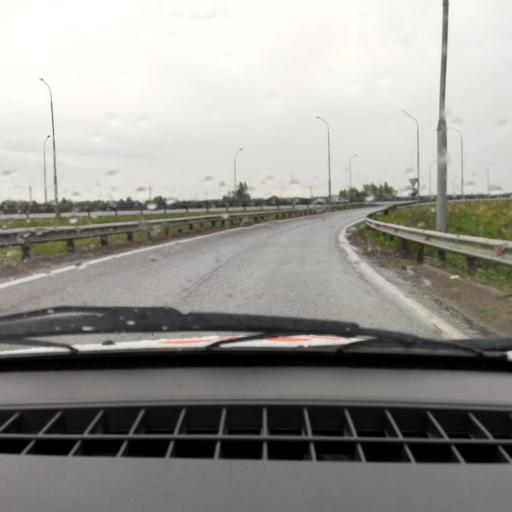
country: RU
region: Bashkortostan
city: Kabakovo
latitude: 54.6659
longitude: 56.1532
